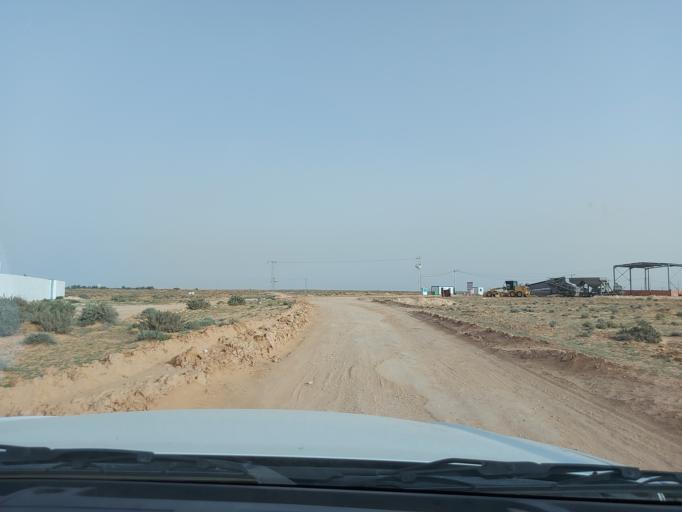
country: TN
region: Madanin
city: Medenine
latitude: 33.2660
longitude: 10.5701
